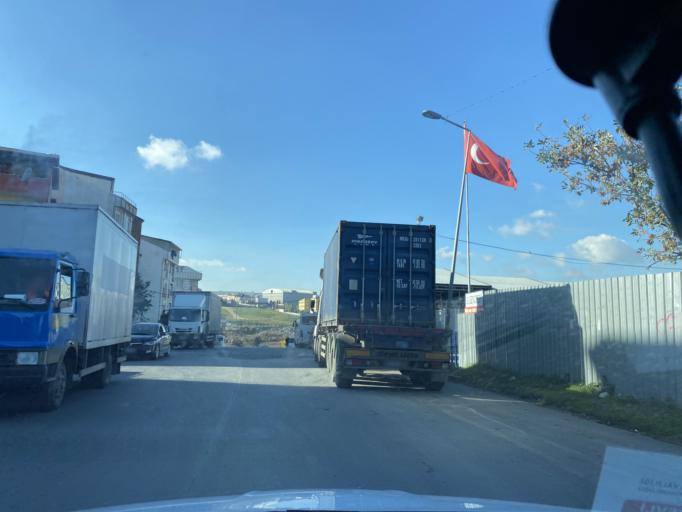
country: TR
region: Istanbul
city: Esenyurt
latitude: 41.0475
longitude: 28.6472
